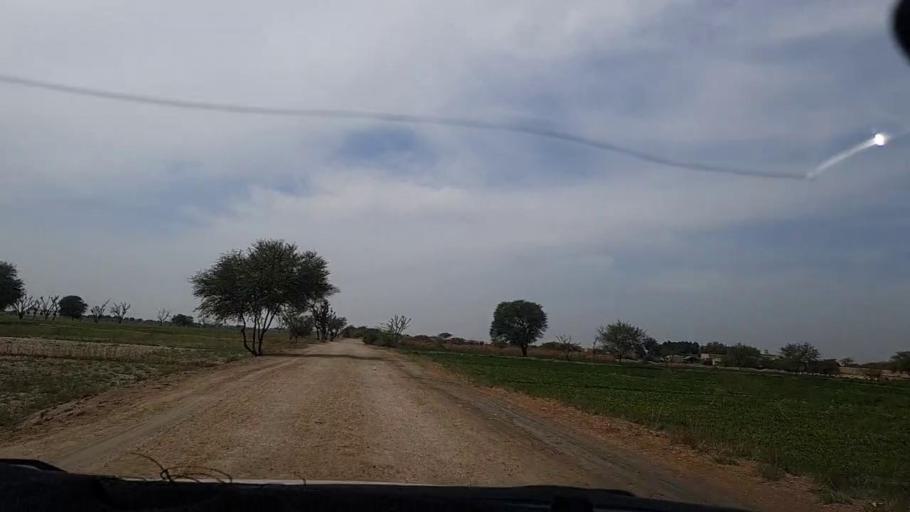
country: PK
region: Sindh
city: Dhoro Naro
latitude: 25.4503
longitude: 69.4960
